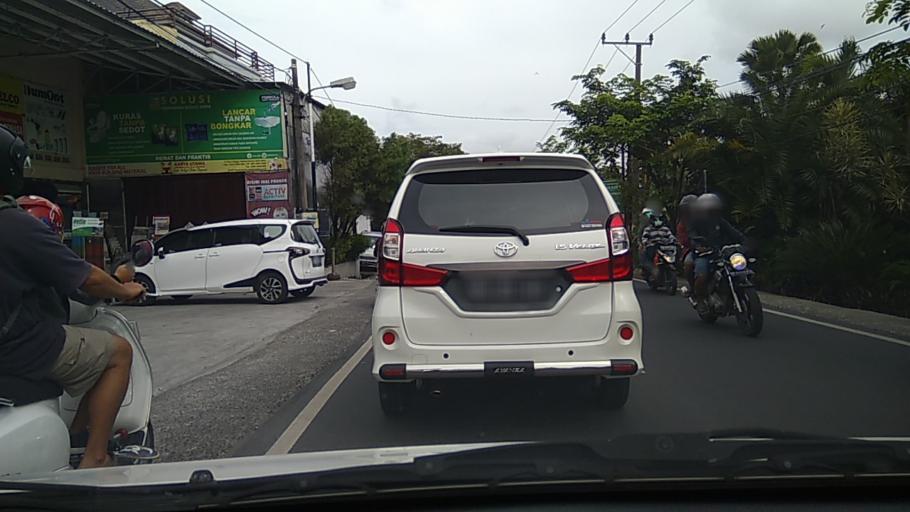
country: ID
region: Bali
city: Banjar Gunungpande
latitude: -8.6409
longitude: 115.1536
